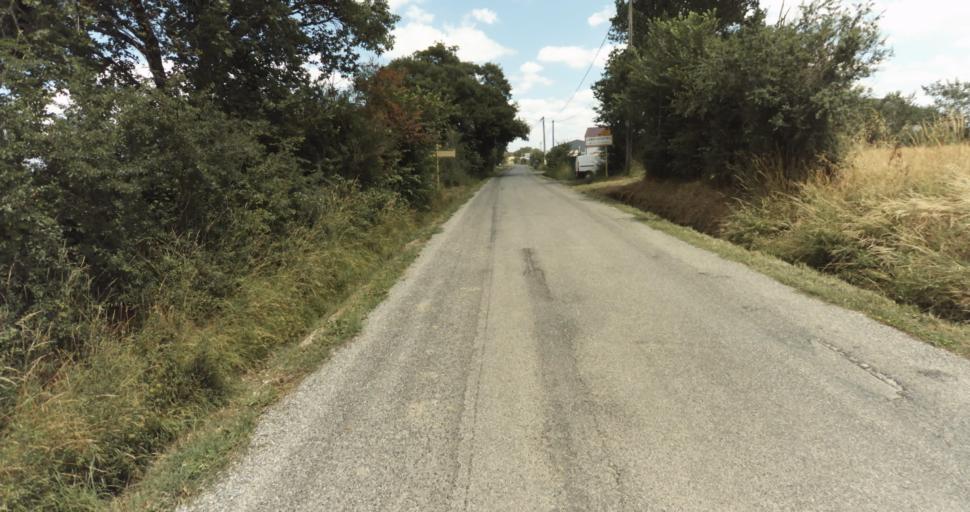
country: FR
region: Midi-Pyrenees
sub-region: Departement de la Haute-Garonne
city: Fontenilles
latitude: 43.5608
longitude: 1.1695
